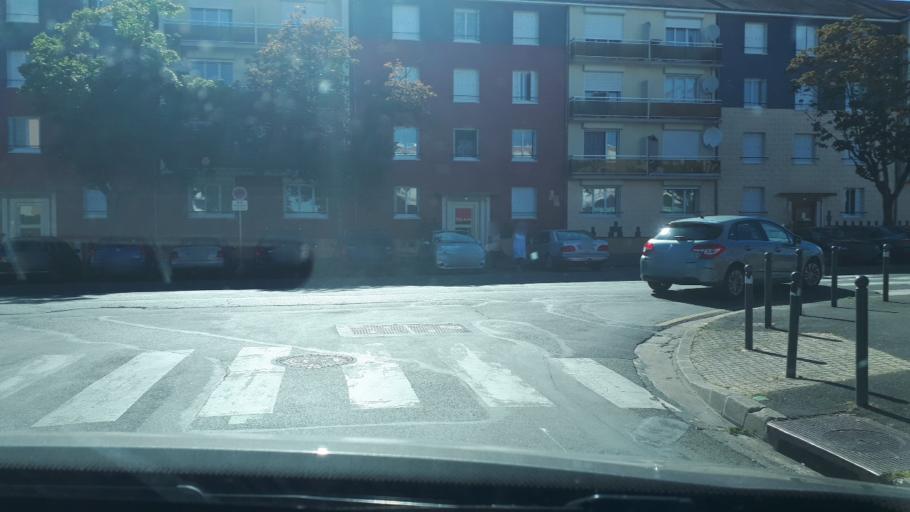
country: FR
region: Centre
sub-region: Departement du Loir-et-Cher
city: Vendome
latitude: 47.8065
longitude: 1.0661
